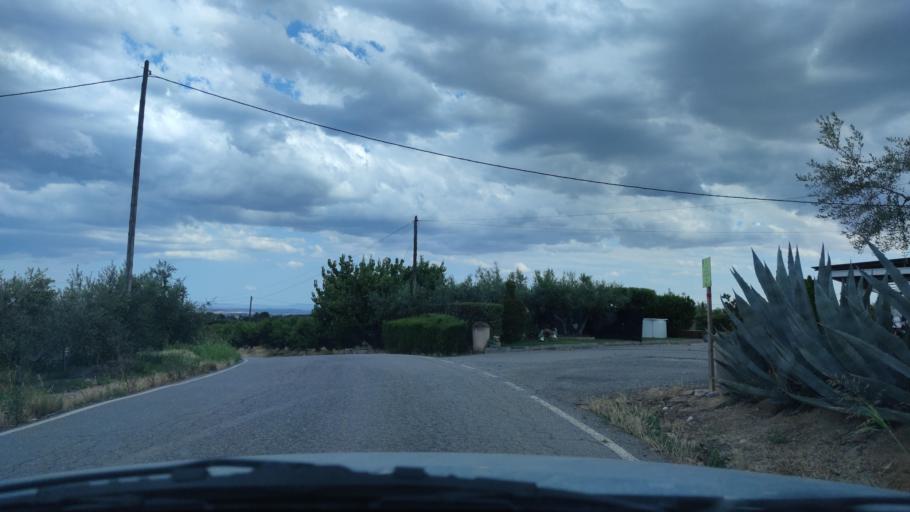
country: ES
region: Catalonia
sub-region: Provincia de Lleida
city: Alpicat
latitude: 41.6261
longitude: 0.5760
